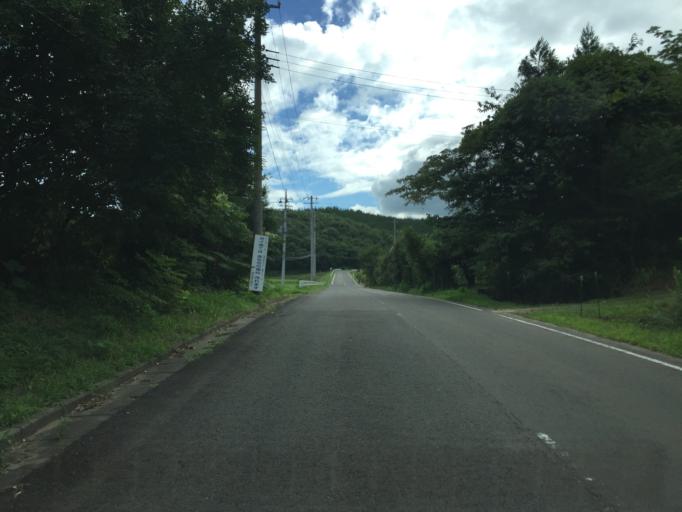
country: JP
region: Fukushima
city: Nihommatsu
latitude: 37.6466
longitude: 140.4179
